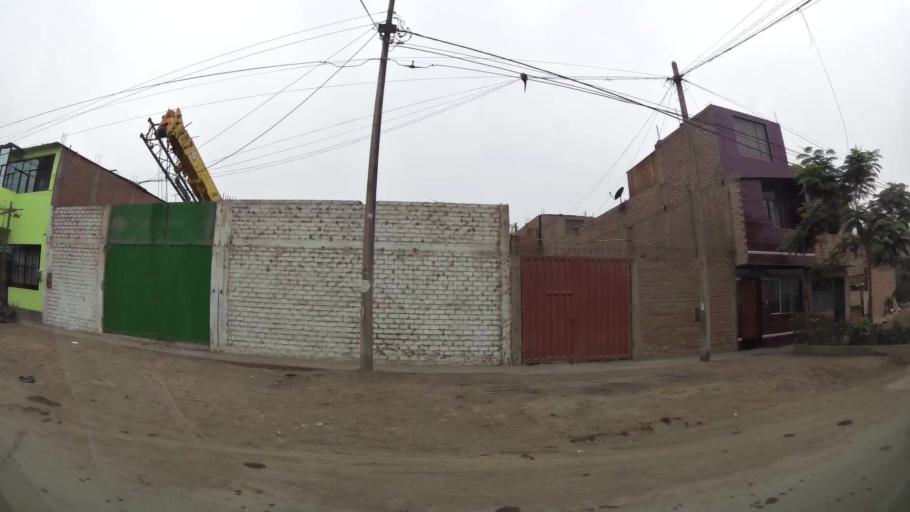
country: PE
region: Lima
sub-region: Lima
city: Urb. Santo Domingo
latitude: -11.8879
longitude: -77.0425
